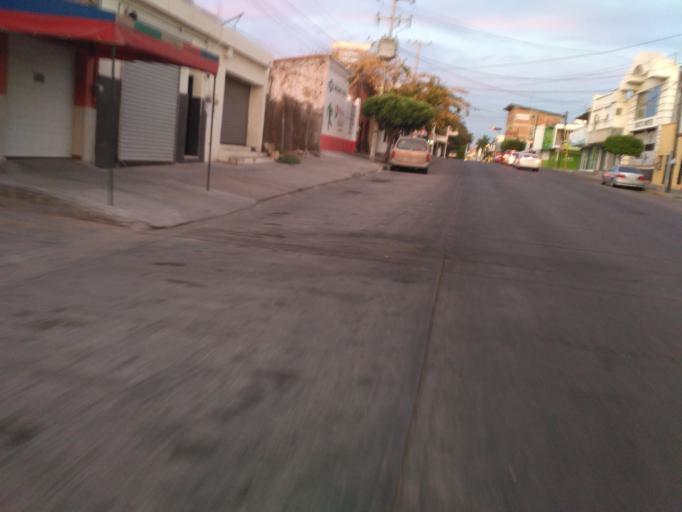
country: MX
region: Sinaloa
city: Culiacan
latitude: 24.8032
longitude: -107.4028
